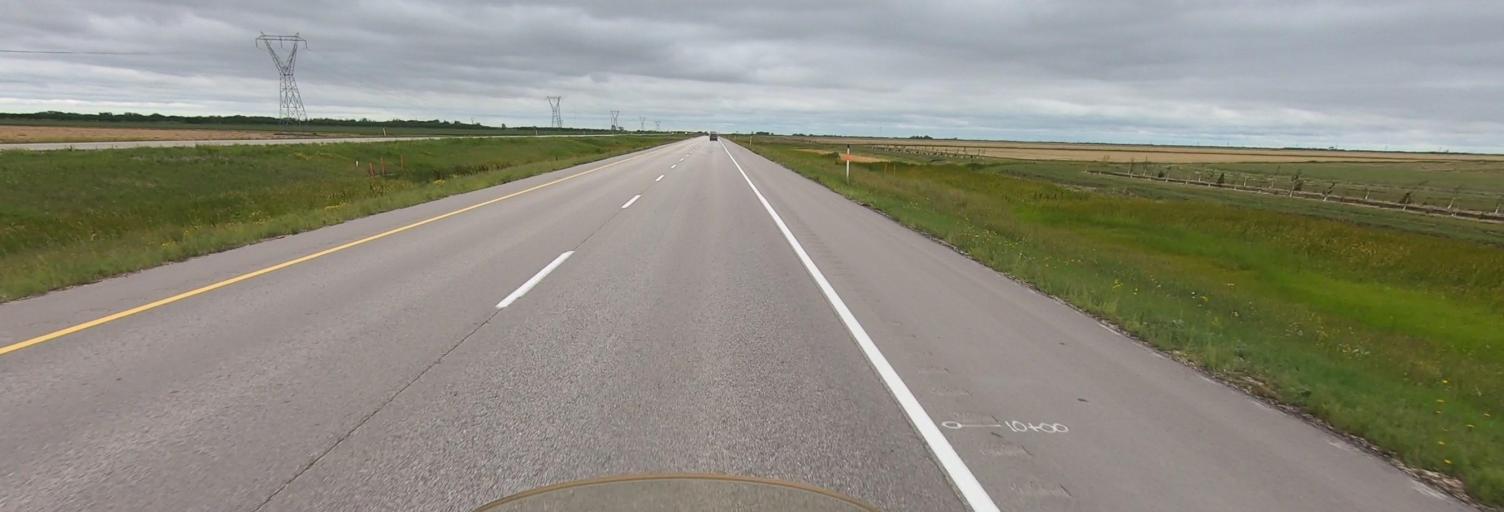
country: CA
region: Manitoba
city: Headingley
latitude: 49.8871
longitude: -97.6142
